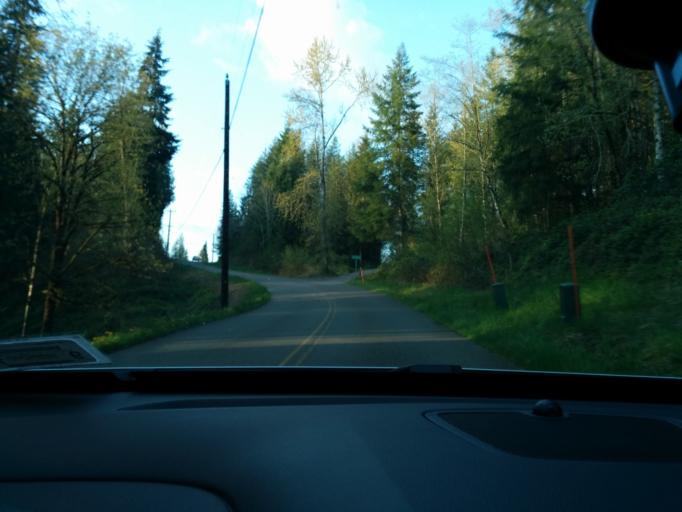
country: US
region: Washington
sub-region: Snohomish County
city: Gold Bar
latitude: 47.8688
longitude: -121.7330
